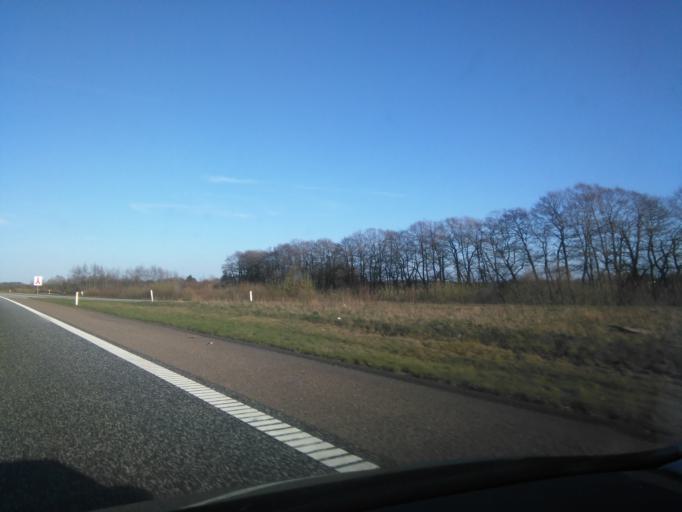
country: DK
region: Central Jutland
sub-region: Herning Kommune
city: Hammerum
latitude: 56.1202
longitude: 9.0515
